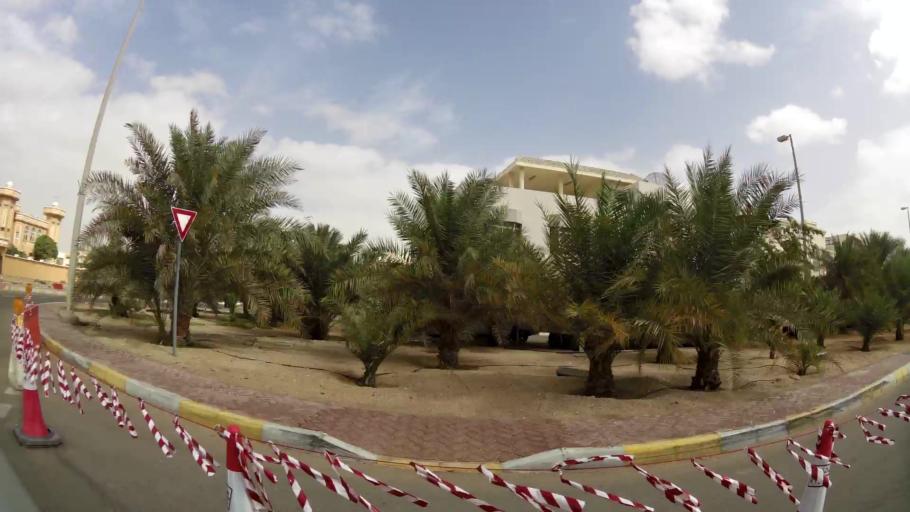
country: AE
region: Abu Dhabi
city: Abu Dhabi
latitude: 24.3993
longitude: 54.5127
